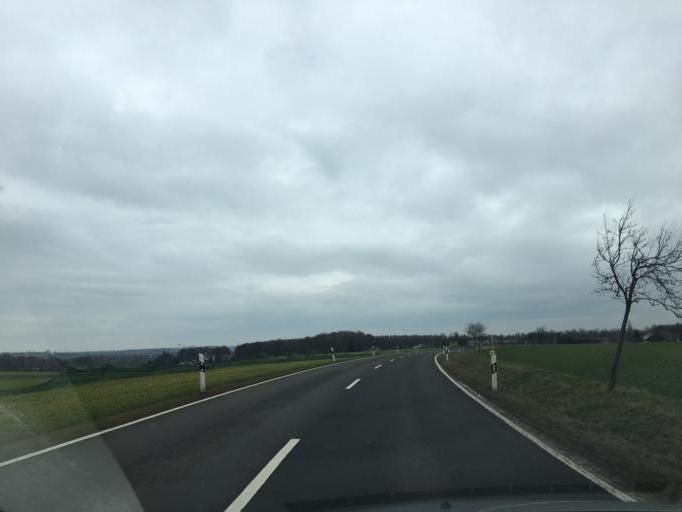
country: DE
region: Thuringia
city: Nobitz
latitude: 50.9531
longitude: 12.5145
